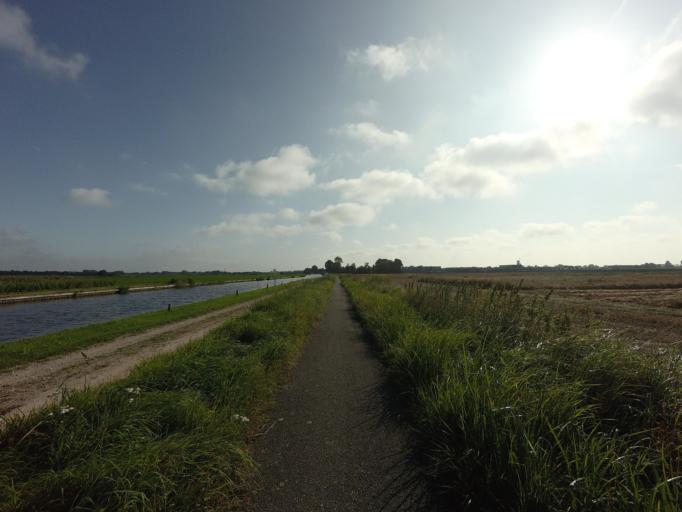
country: NL
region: Overijssel
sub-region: Gemeente Steenwijkerland
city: Tuk
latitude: 52.7833
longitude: 6.0780
